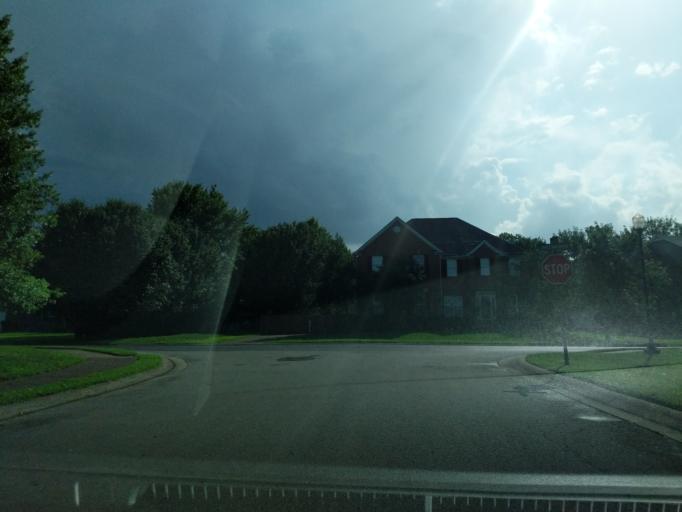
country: US
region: Tennessee
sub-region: Cheatham County
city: Pegram
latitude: 36.0372
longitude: -86.9566
